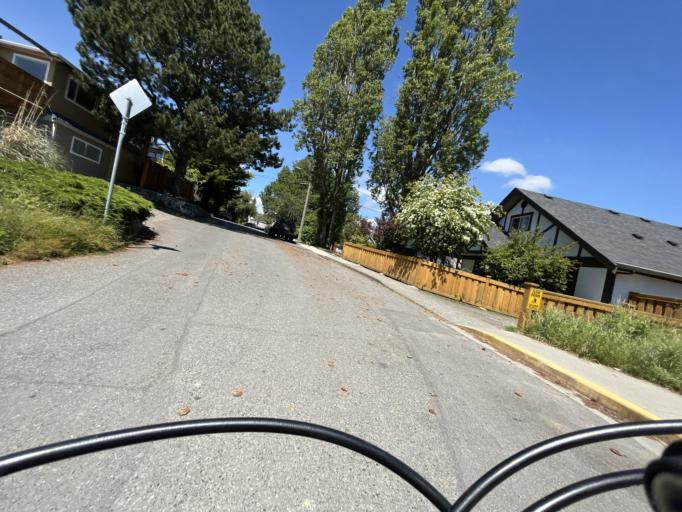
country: CA
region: British Columbia
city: Victoria
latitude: 48.4393
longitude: -123.3888
